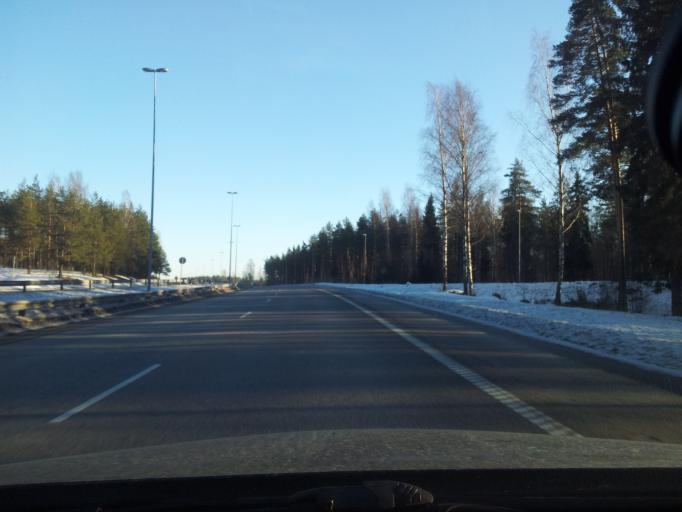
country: FI
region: Uusimaa
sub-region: Helsinki
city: Kirkkonummi
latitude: 60.2734
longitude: 24.4542
